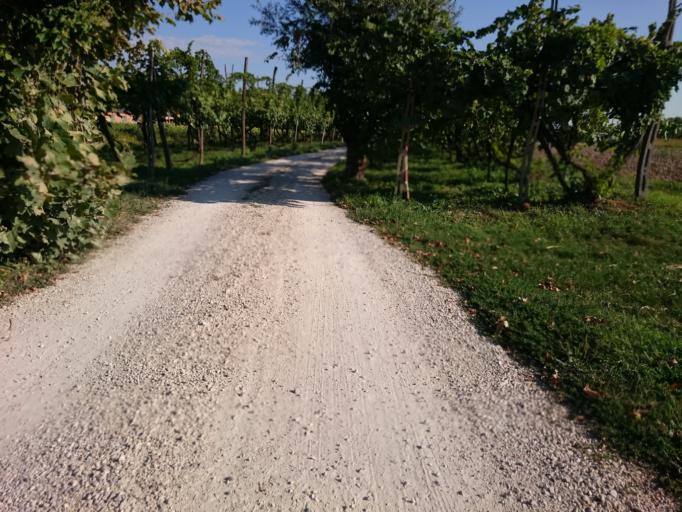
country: IT
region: Veneto
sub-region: Provincia di Padova
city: Albignasego
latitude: 45.3418
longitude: 11.8958
